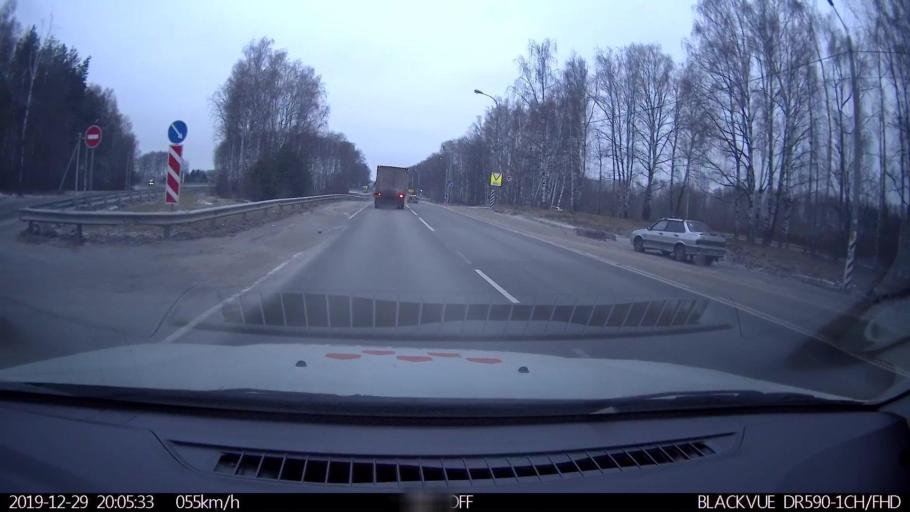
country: RU
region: Nizjnij Novgorod
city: Neklyudovo
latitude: 56.3923
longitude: 44.0103
